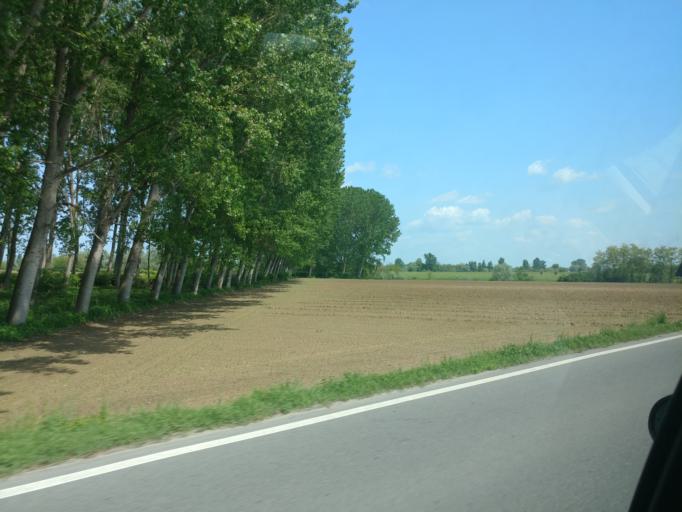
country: IT
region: Piedmont
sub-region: Provincia di Cuneo
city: Carde
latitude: 44.7269
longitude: 7.4318
